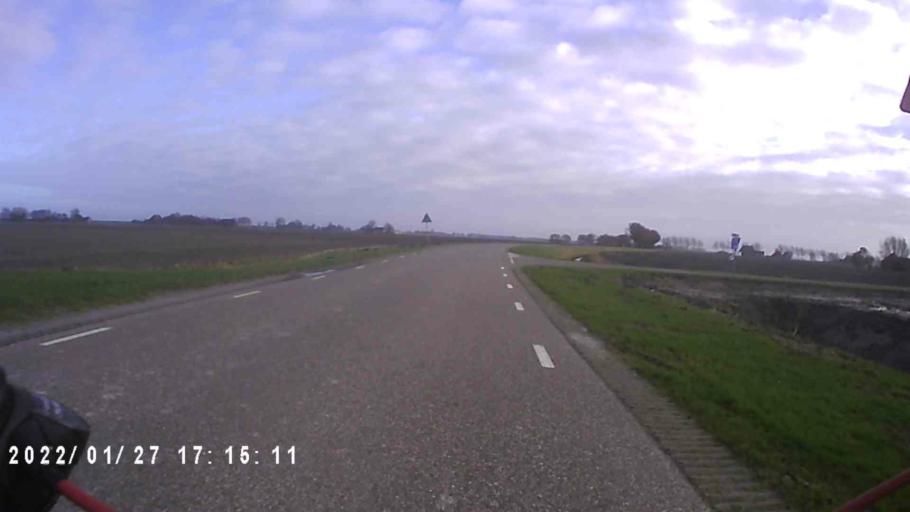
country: NL
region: Friesland
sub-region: Gemeente Dongeradeel
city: Anjum
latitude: 53.3942
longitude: 6.0970
